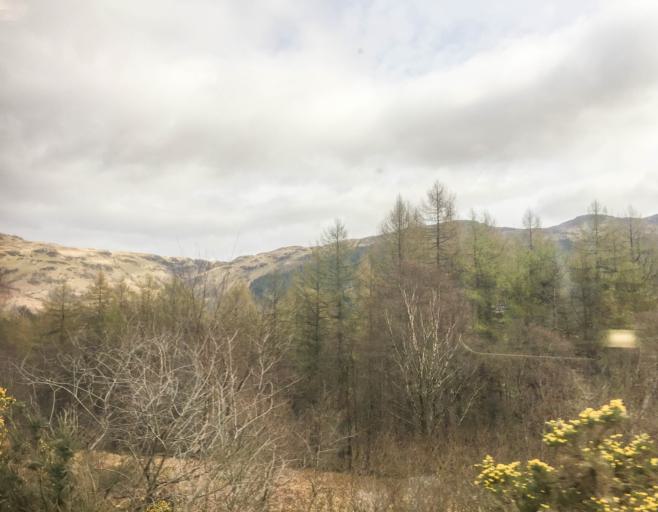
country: GB
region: Scotland
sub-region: Argyll and Bute
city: Garelochhead
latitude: 56.2137
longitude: -4.7002
